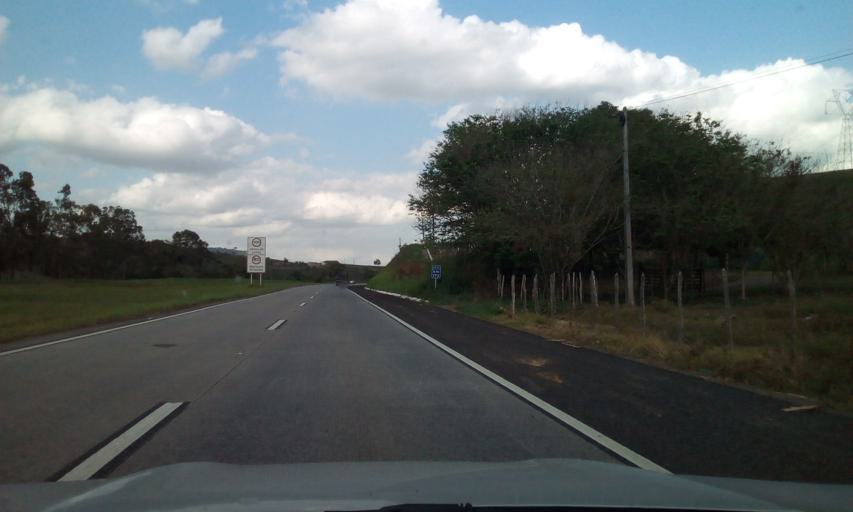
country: BR
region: Pernambuco
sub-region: Joaquim Nabuco
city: Joaquim Nabuco
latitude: -8.5962
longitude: -35.5263
